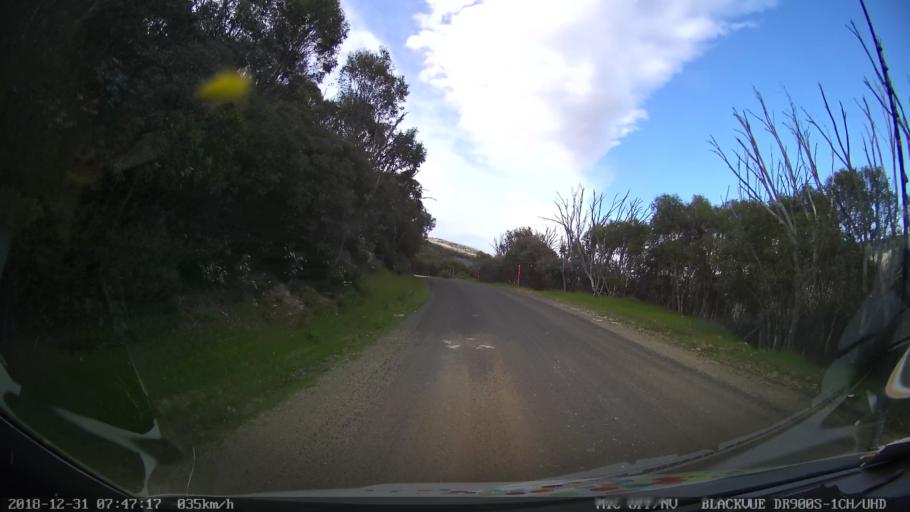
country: AU
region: New South Wales
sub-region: Snowy River
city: Jindabyne
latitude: -36.3630
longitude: 148.3965
